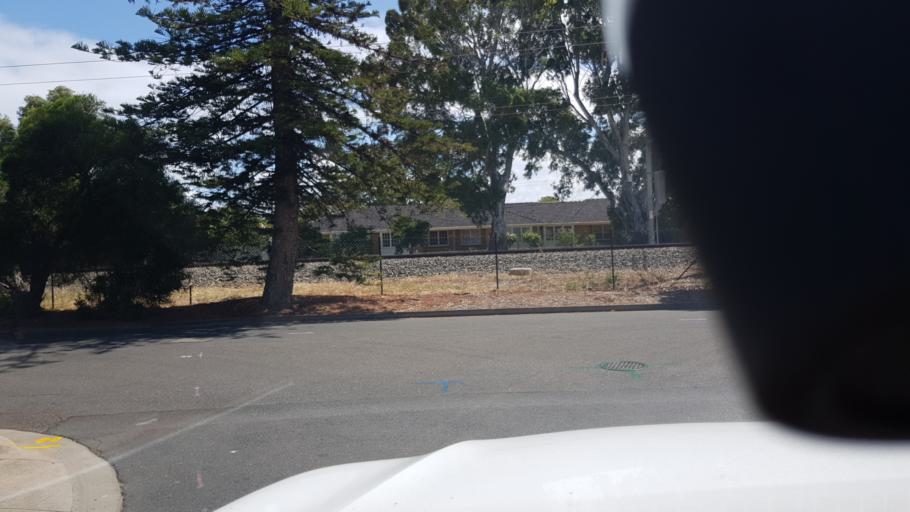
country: AU
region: South Australia
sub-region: Adelaide
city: Brighton
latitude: -35.0123
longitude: 138.5265
